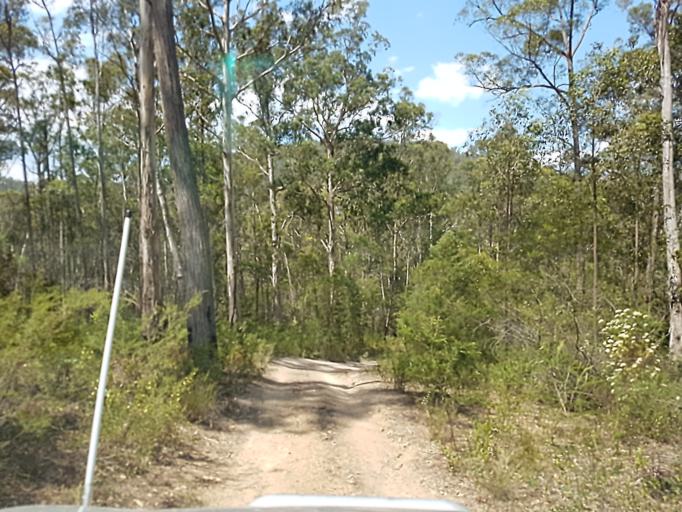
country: AU
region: Victoria
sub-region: East Gippsland
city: Lakes Entrance
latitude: -37.4082
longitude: 148.3089
